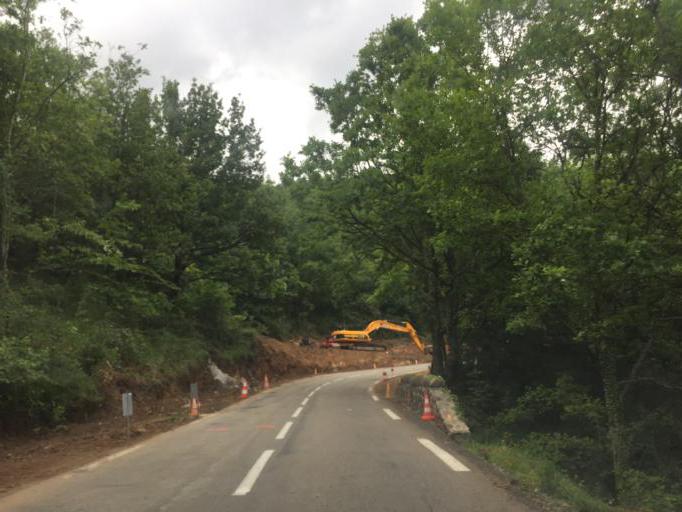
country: FR
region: Rhone-Alpes
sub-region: Departement de l'Ardeche
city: Privas
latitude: 44.7442
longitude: 4.6056
